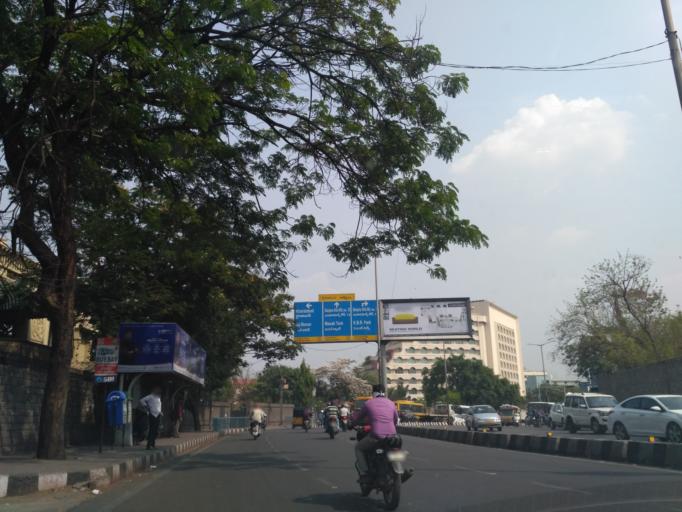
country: IN
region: Telangana
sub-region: Hyderabad
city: Hyderabad
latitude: 17.4183
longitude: 78.4487
